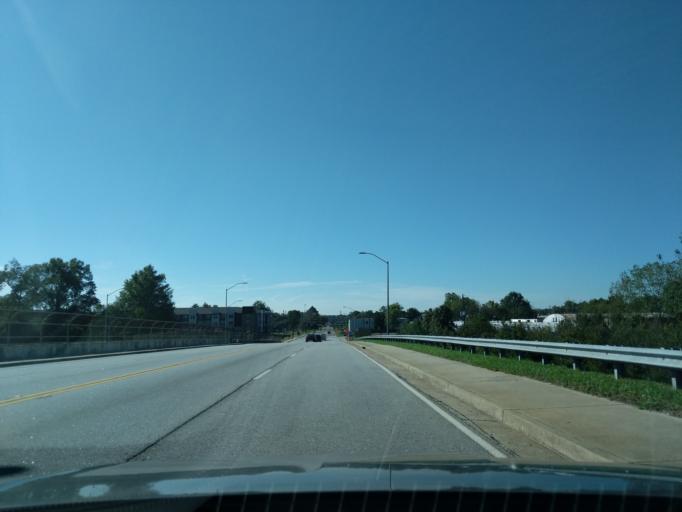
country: US
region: Georgia
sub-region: Richmond County
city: Augusta
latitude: 33.4637
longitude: -81.9950
